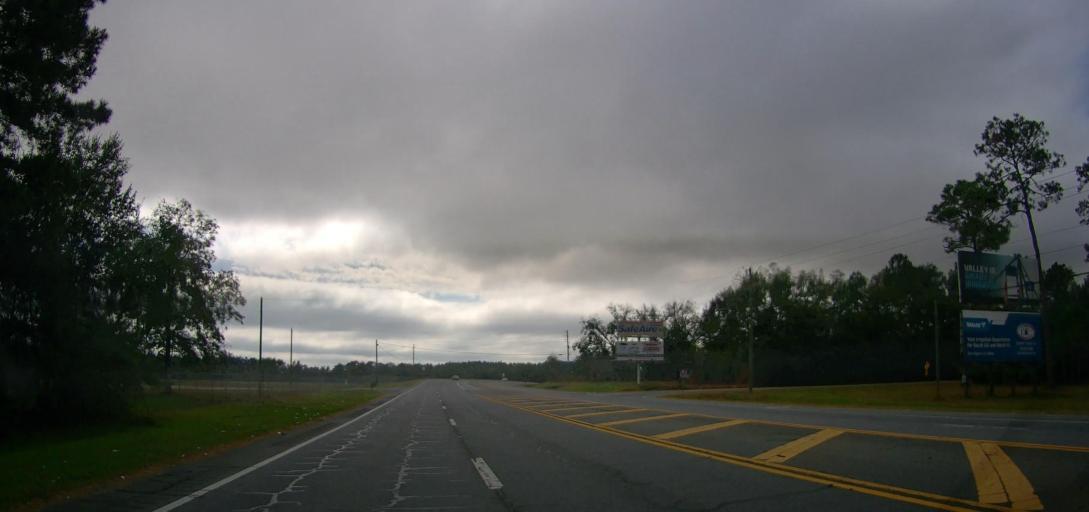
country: US
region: Georgia
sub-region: Colquitt County
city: Moultrie
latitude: 31.2249
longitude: -83.7495
